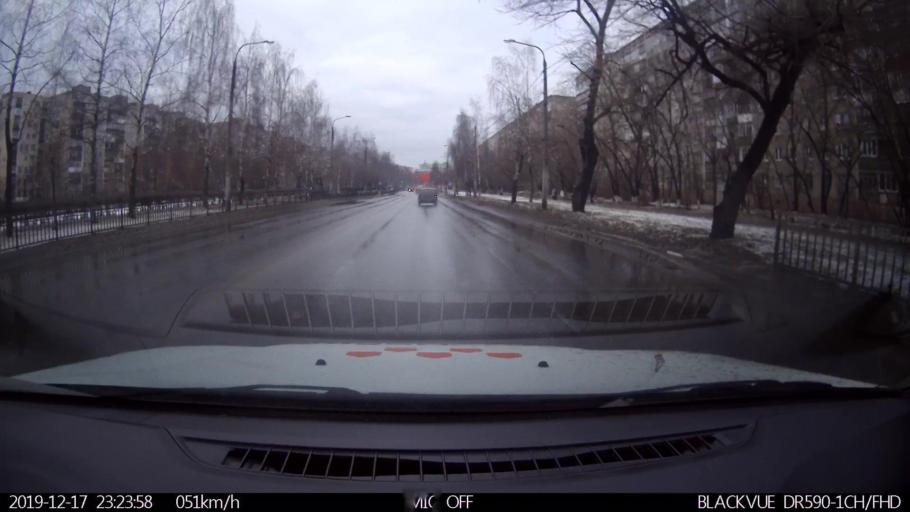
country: RU
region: Nizjnij Novgorod
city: Gorbatovka
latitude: 56.3604
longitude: 43.8221
